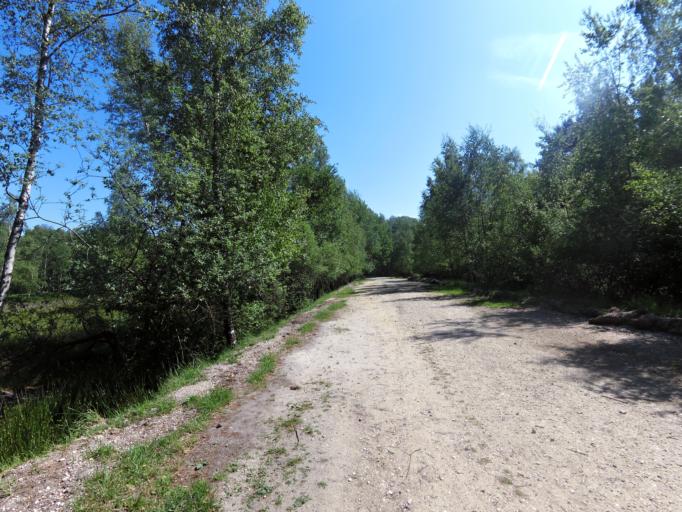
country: NL
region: Limburg
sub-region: Gemeente Onderbanken
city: Schinveld
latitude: 50.9508
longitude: 6.0238
